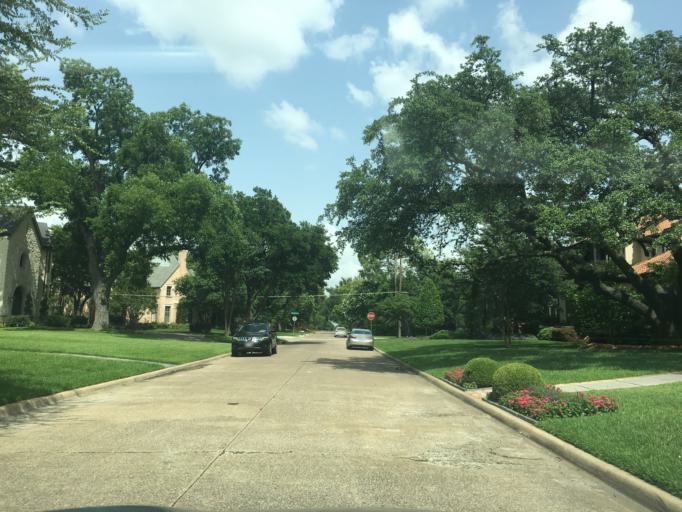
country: US
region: Texas
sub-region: Dallas County
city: University Park
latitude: 32.8884
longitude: -96.7941
